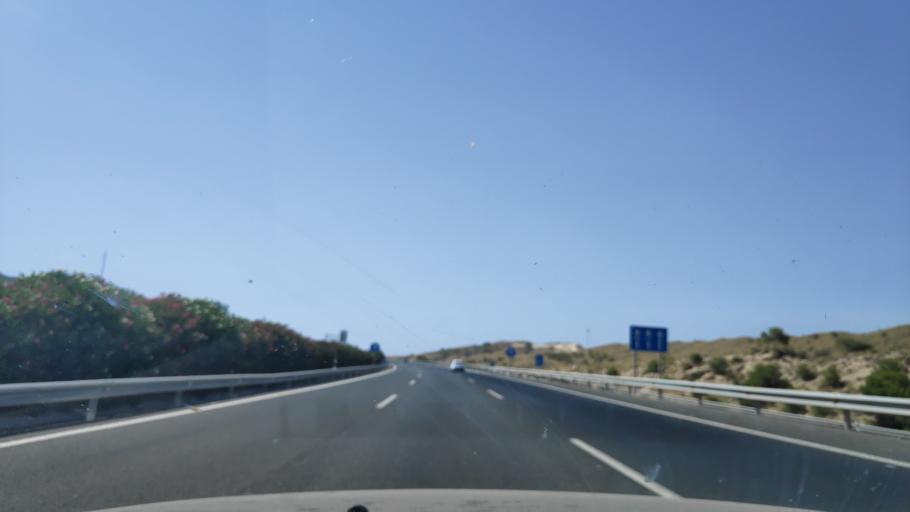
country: ES
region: Murcia
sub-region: Murcia
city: Ulea
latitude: 38.1604
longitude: -1.2996
